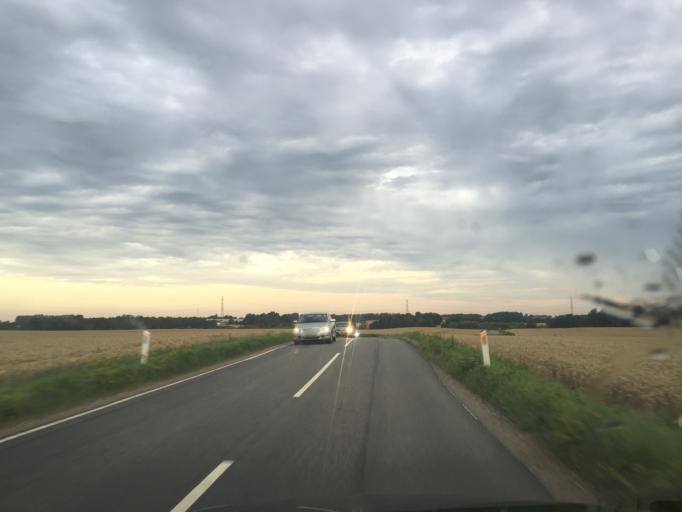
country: DK
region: Capital Region
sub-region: Hoje-Taastrup Kommune
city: Flong
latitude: 55.6946
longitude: 12.2372
